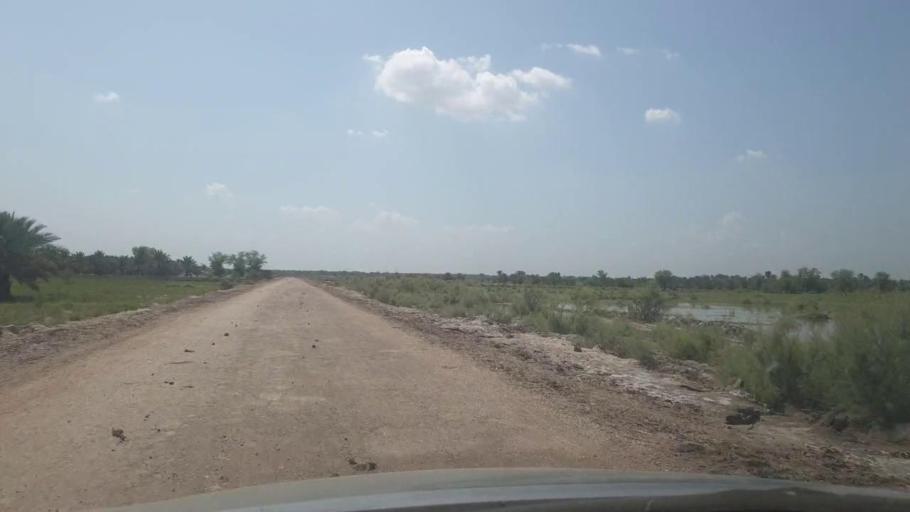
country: PK
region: Sindh
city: Khairpur
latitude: 27.5242
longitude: 68.8147
